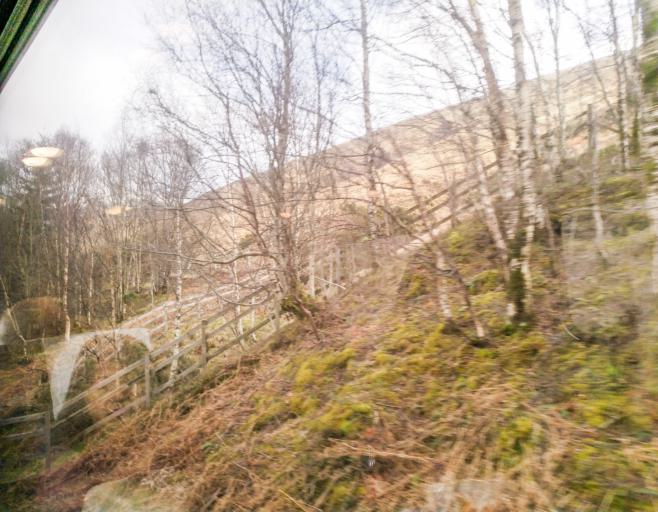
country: GB
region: Scotland
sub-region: Highland
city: Spean Bridge
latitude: 56.8036
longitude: -4.7195
